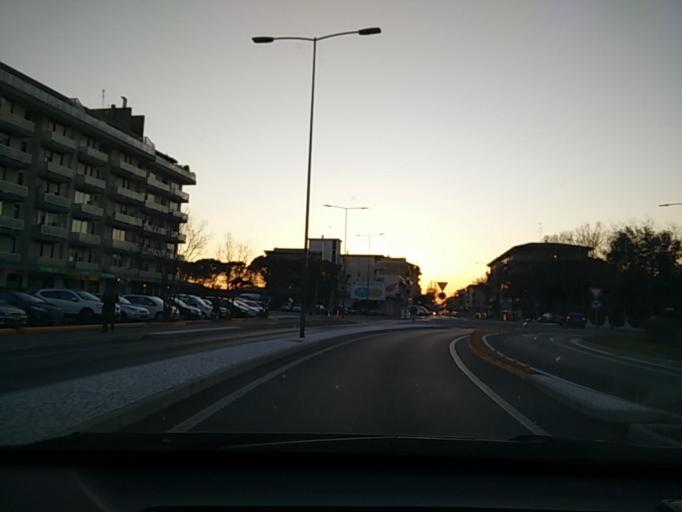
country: IT
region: Veneto
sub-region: Provincia di Venezia
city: San Dona di Piave
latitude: 45.6309
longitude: 12.5849
